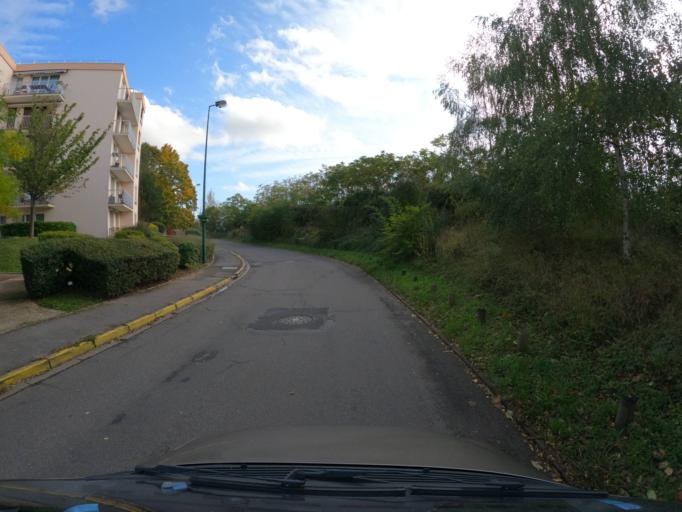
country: FR
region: Ile-de-France
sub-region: Departement de Seine-et-Marne
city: Vaires-sur-Marne
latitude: 48.8759
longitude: 2.6424
